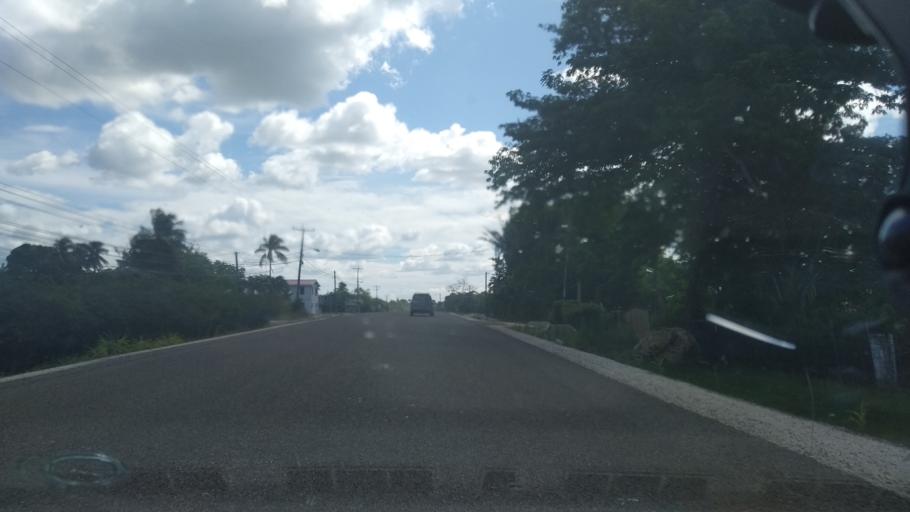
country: BZ
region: Cayo
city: Belmopan
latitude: 17.2512
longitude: -88.8140
